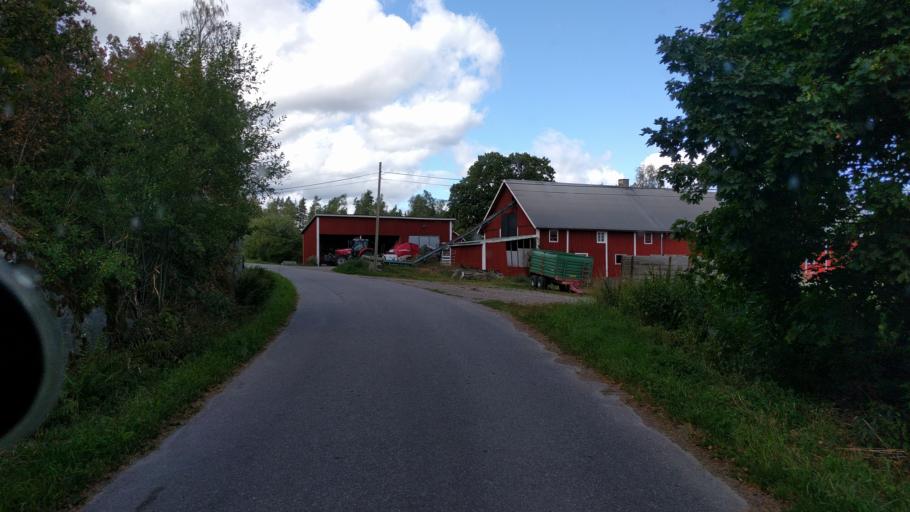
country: SE
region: Kalmar
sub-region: Vasterviks Kommun
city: Ankarsrum
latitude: 57.8015
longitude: 16.1721
